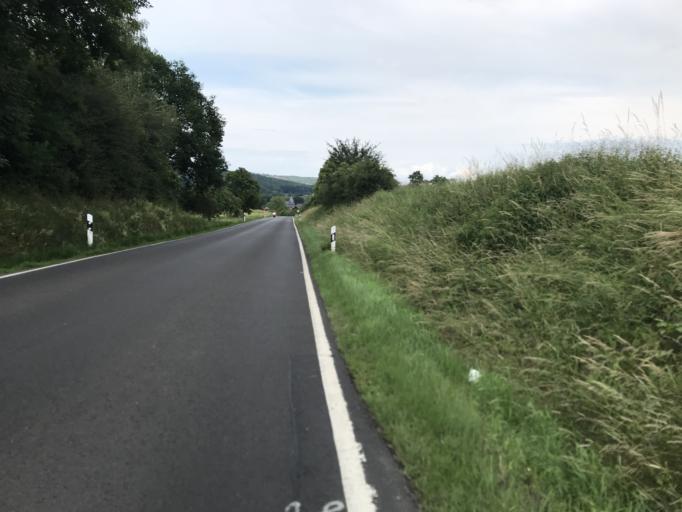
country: DE
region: Hesse
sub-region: Regierungsbezirk Giessen
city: Laubach
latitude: 50.5365
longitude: 8.9819
